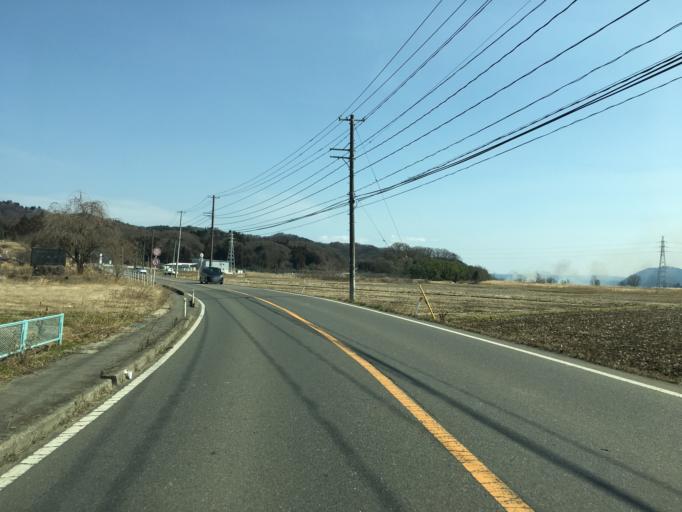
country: JP
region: Fukushima
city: Ishikawa
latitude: 37.1310
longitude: 140.2753
